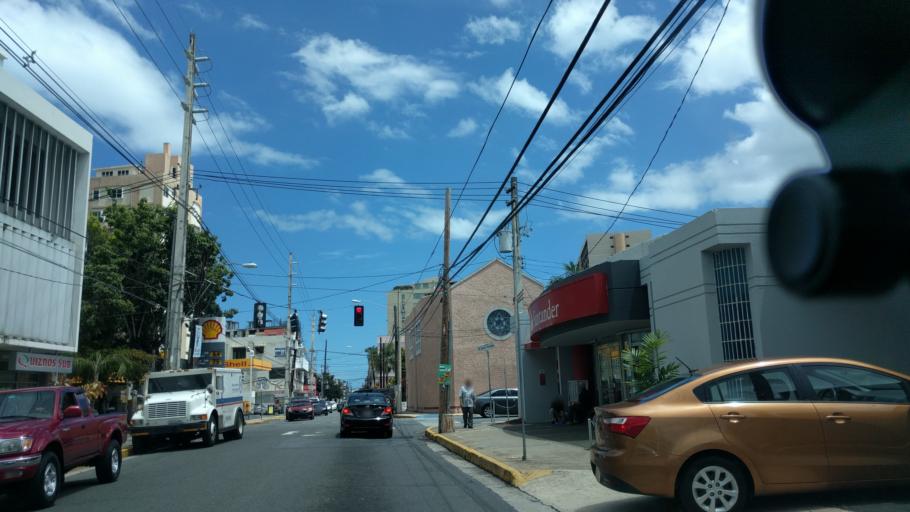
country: PR
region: San Juan
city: San Juan
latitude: 18.4518
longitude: -66.0620
